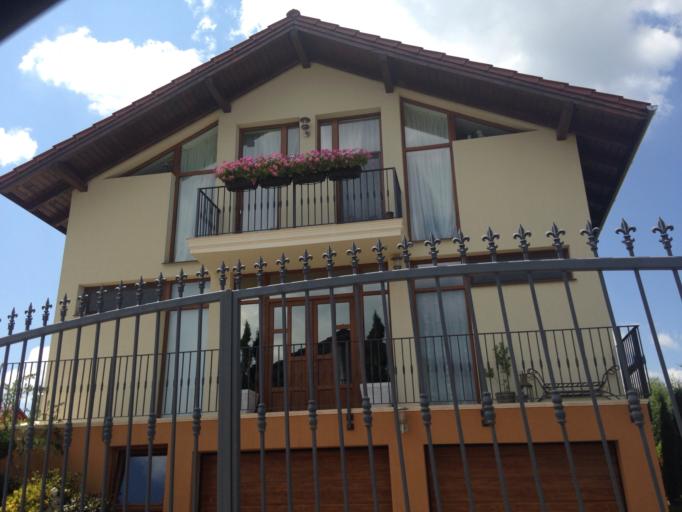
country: RO
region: Cluj
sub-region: Comuna Feleacu
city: Feleacu
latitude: 46.7326
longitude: 23.5901
